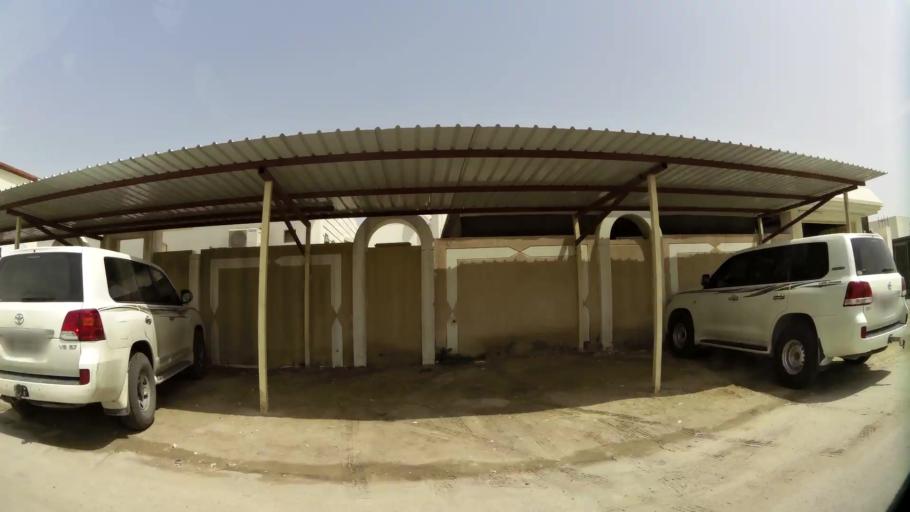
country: QA
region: Baladiyat ar Rayyan
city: Ar Rayyan
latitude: 25.2316
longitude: 51.4185
